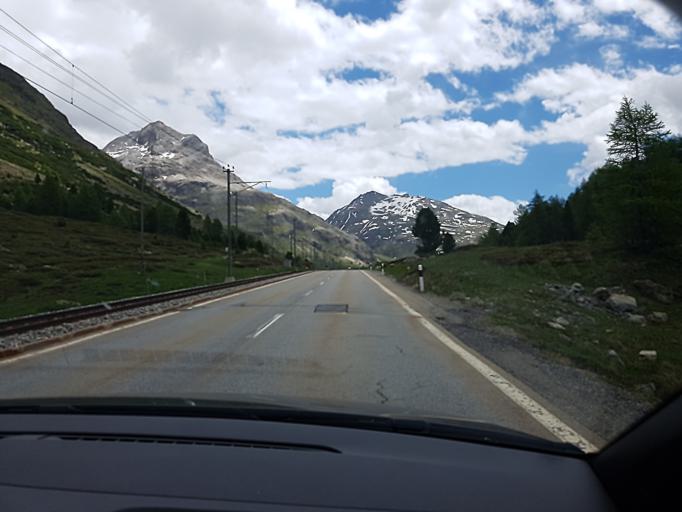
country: CH
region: Grisons
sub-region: Maloja District
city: Pontresina
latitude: 46.4486
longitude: 9.9581
